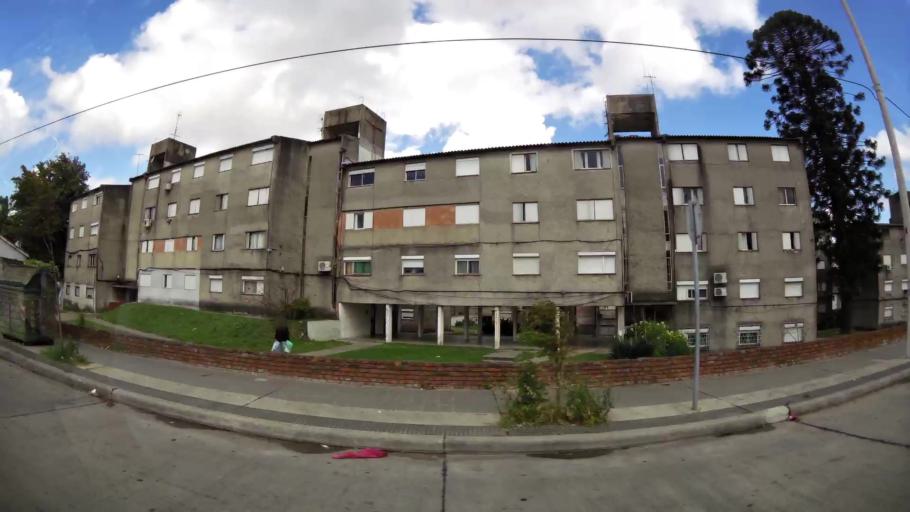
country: UY
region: Montevideo
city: Montevideo
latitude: -34.8498
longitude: -56.2236
